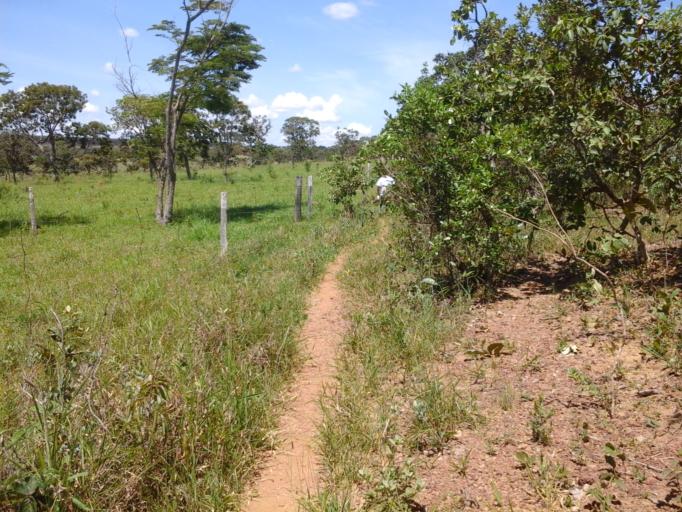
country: BR
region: Goias
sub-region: Abadiania
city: Abadiania
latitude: -15.9776
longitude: -48.5306
